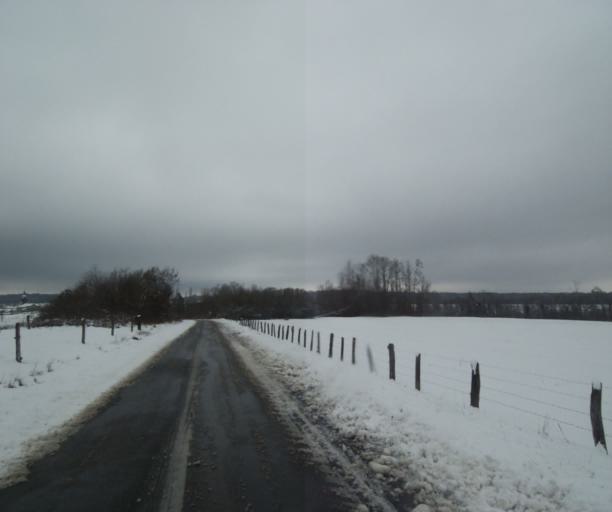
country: FR
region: Champagne-Ardenne
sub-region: Departement de la Haute-Marne
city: Laneuville-a-Remy
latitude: 48.4590
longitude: 4.9242
